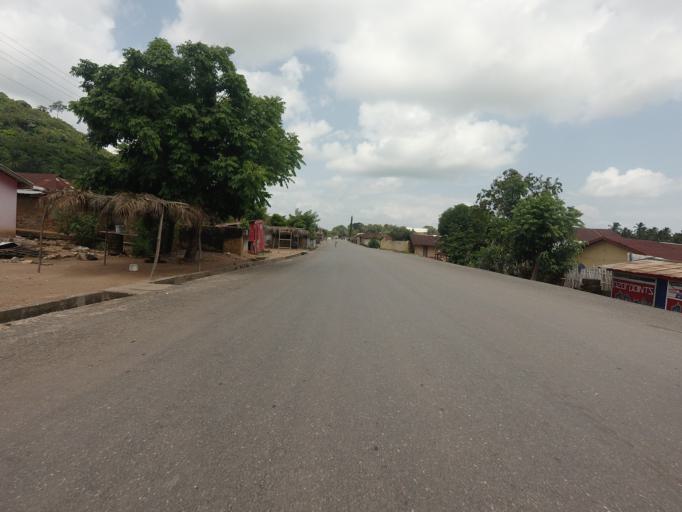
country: GH
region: Volta
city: Ho
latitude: 6.7400
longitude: 0.3500
